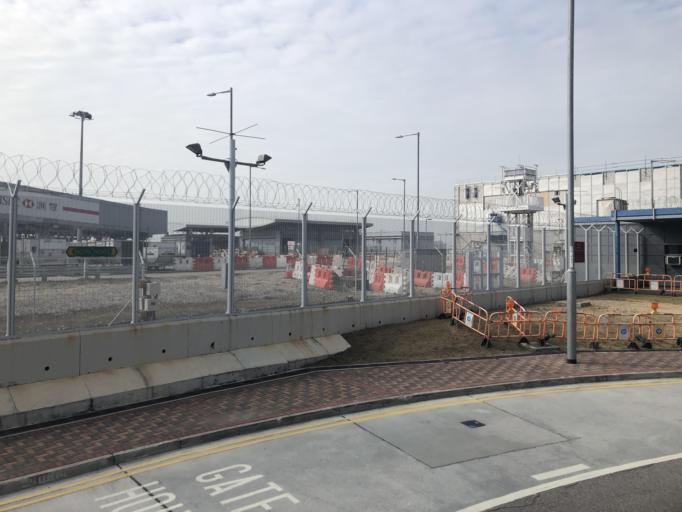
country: HK
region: Tuen Mun
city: Tuen Mun
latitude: 22.3190
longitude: 113.9334
